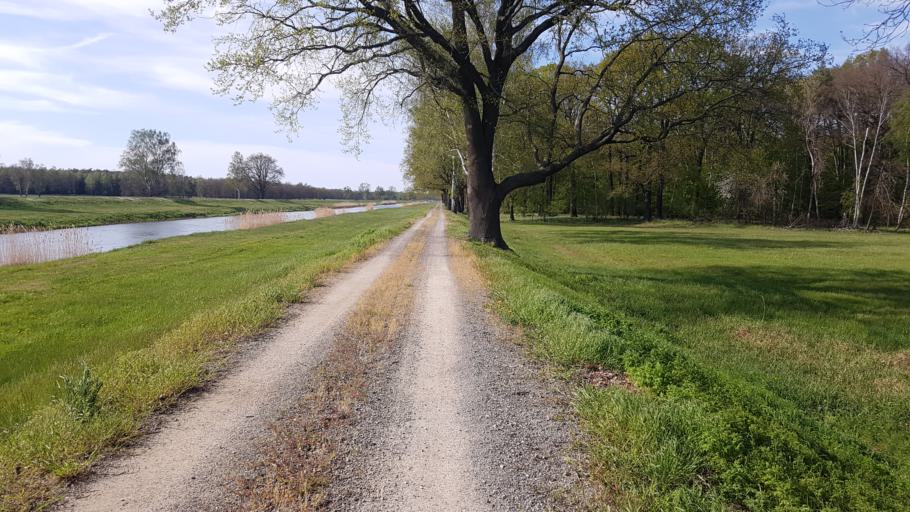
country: DE
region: Brandenburg
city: Falkenberg
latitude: 51.6222
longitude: 13.2879
